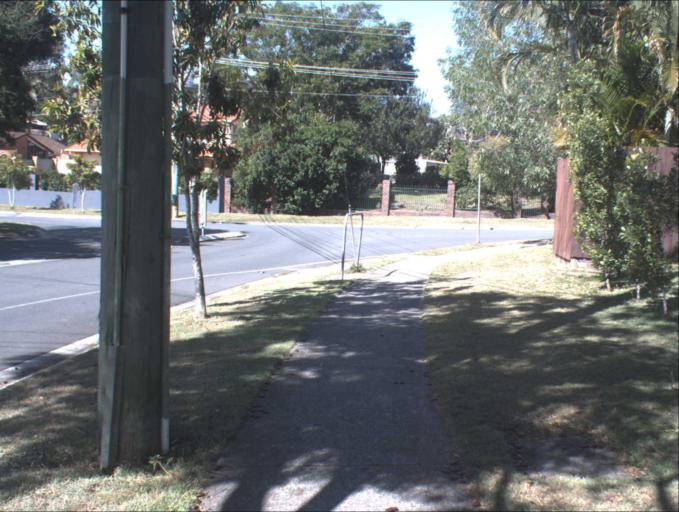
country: AU
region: Queensland
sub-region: Logan
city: Rochedale South
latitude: -27.5942
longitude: 153.1367
